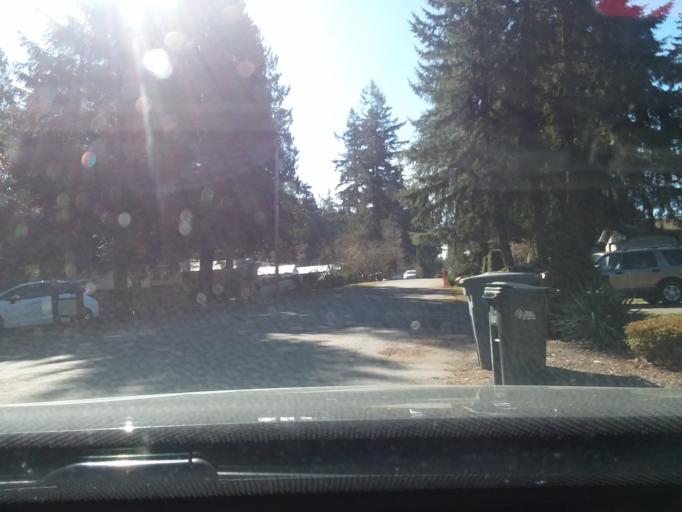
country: US
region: Washington
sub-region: Pierce County
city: Summit
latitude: 47.1662
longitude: -122.3437
